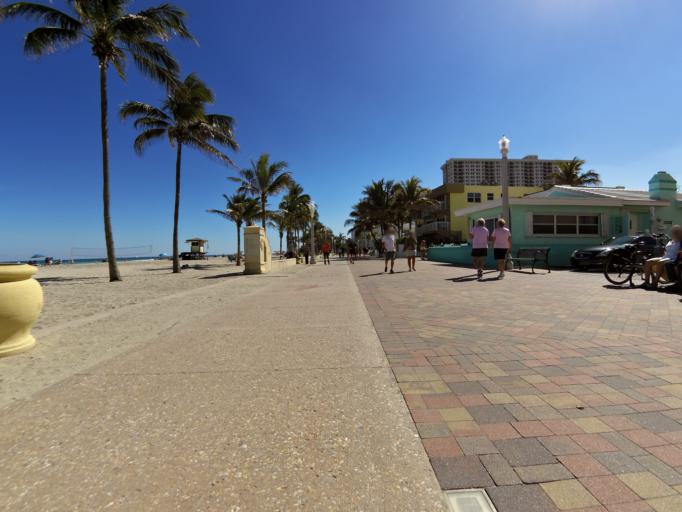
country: US
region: Florida
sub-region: Broward County
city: Hollywood
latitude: 26.0084
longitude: -80.1160
